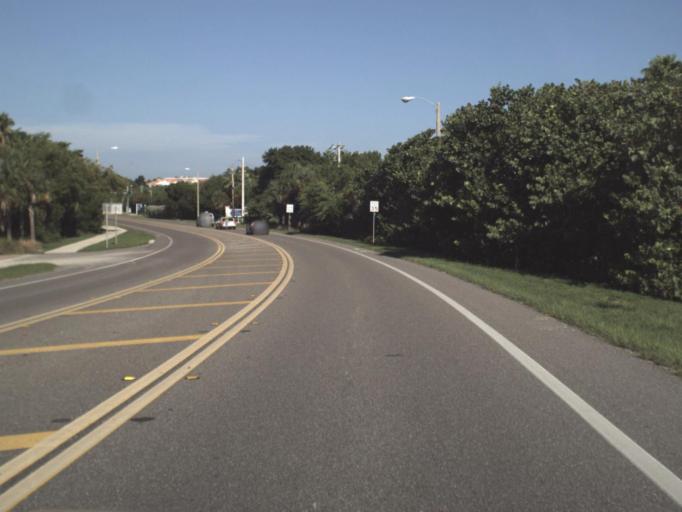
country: US
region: Florida
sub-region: Sarasota County
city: Siesta Key
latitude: 27.3352
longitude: -82.5837
